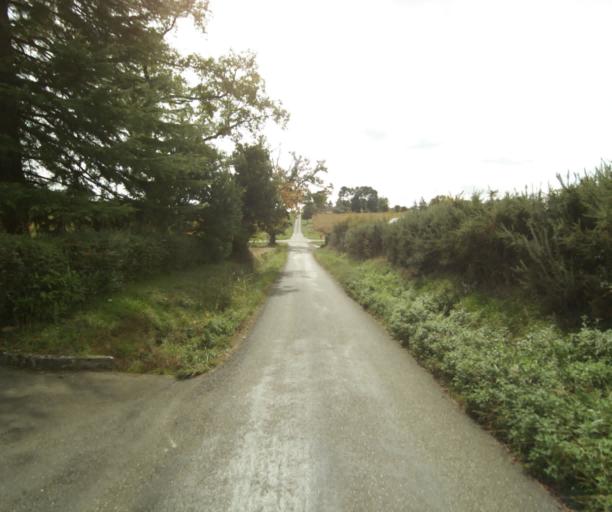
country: FR
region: Midi-Pyrenees
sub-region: Departement du Gers
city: Eauze
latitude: 43.8562
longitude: 0.0772
